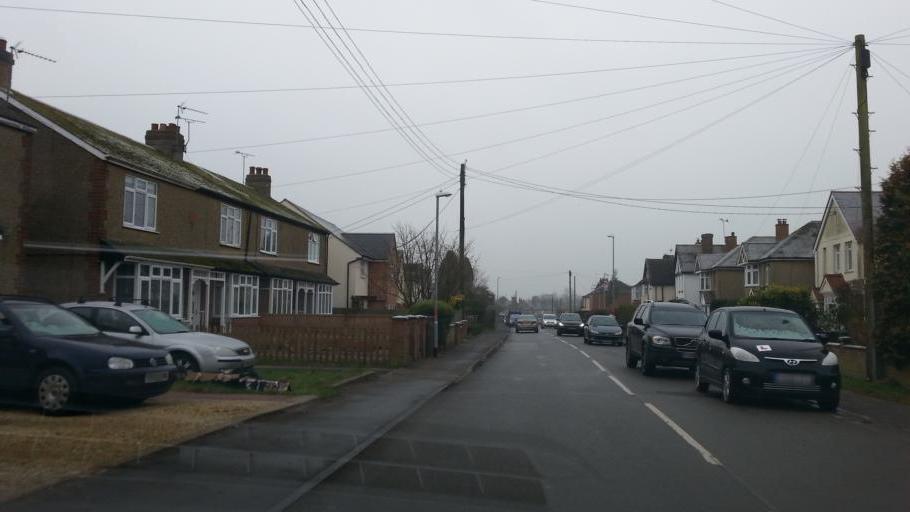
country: GB
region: England
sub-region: Northamptonshire
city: Brackley
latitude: 52.0364
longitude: -1.1474
